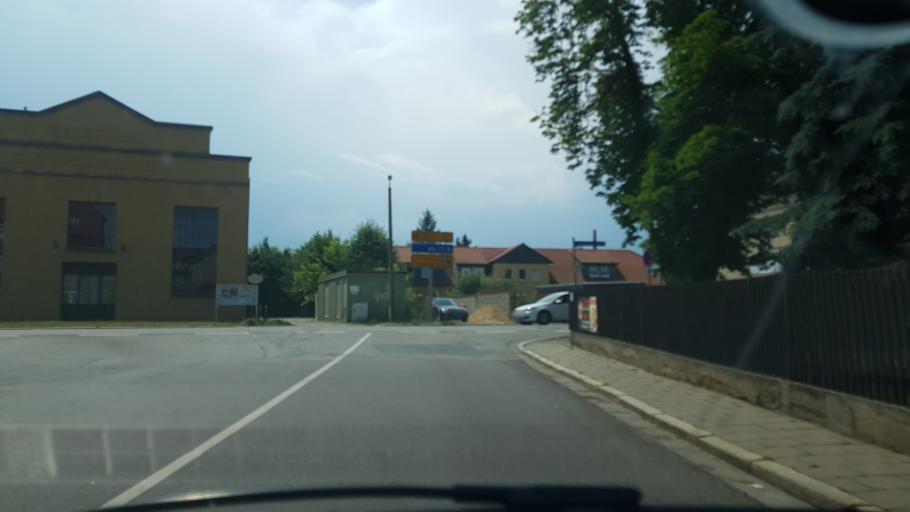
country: DE
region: Saxony-Anhalt
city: Osterwieck
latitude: 51.9673
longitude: 10.7142
